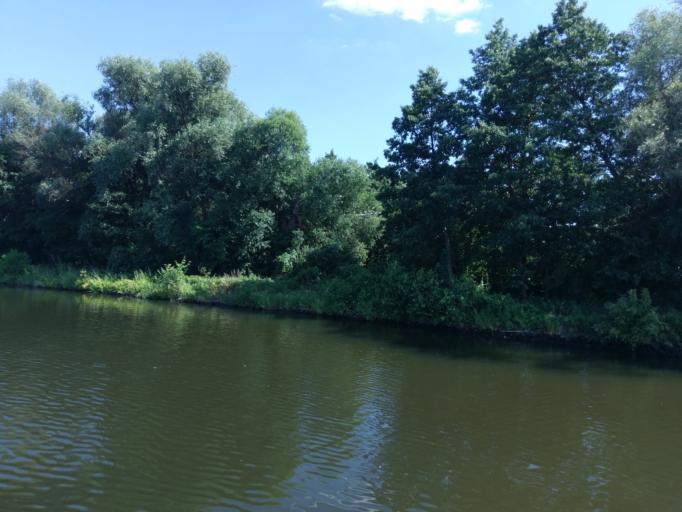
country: DE
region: Brandenburg
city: Brandenburg an der Havel
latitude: 52.4207
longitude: 12.5863
